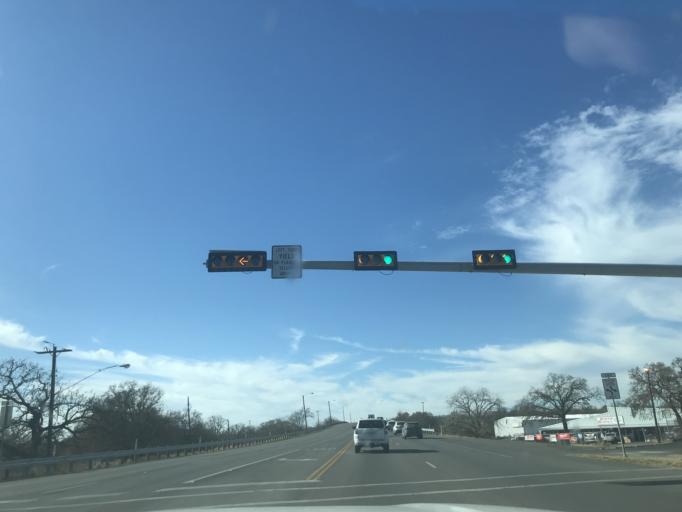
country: US
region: Texas
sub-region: Erath County
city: Stephenville
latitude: 32.2048
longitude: -98.2153
